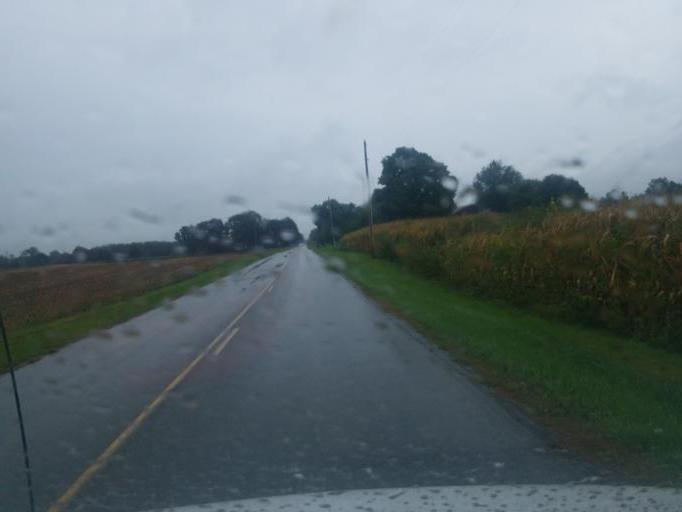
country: US
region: Ohio
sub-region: Medina County
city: Seville
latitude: 40.9884
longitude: -81.8588
